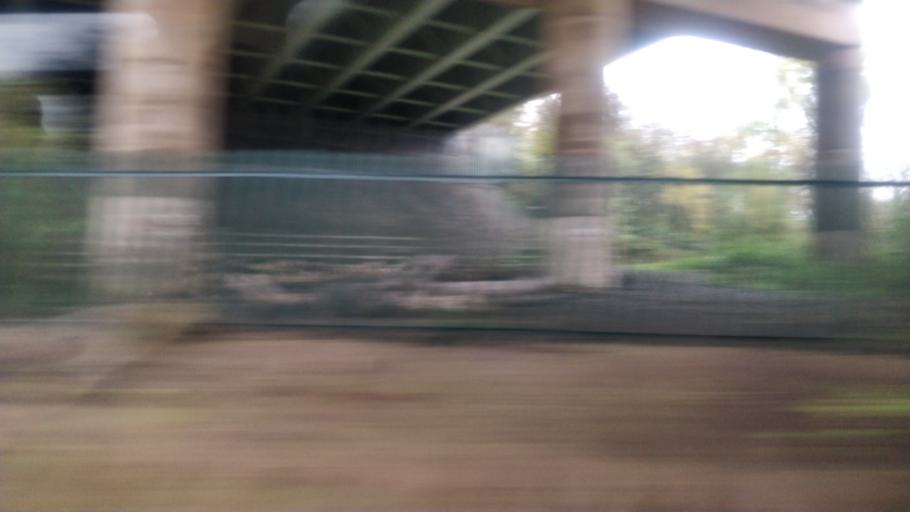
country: GB
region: England
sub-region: Borough of Wigan
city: Shevington
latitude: 53.5619
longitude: -2.7014
